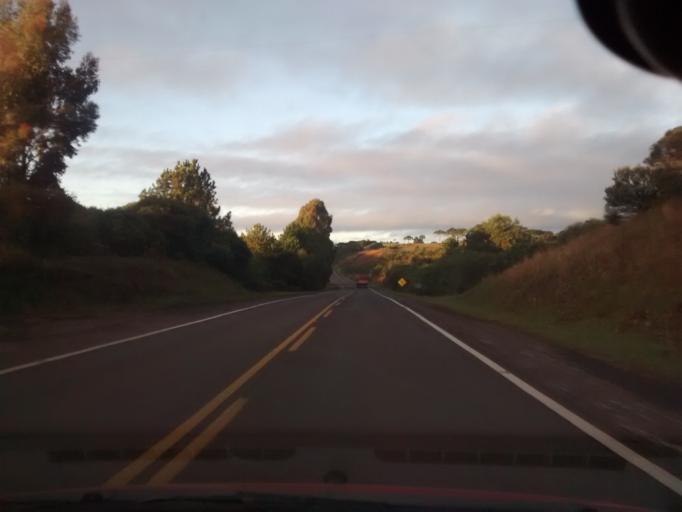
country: BR
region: Rio Grande do Sul
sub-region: Vacaria
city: Vacaria
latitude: -28.3136
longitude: -50.8037
